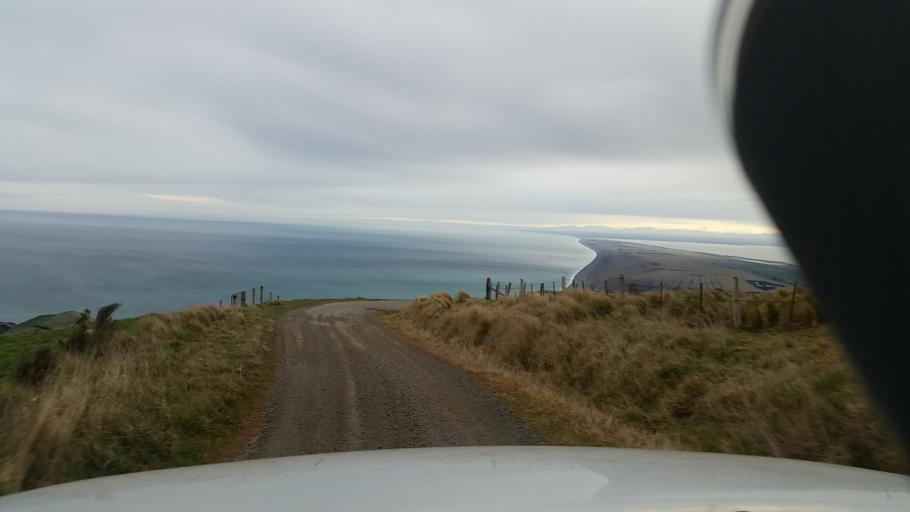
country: NZ
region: Canterbury
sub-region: Christchurch City
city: Christchurch
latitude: -43.8207
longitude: 172.7705
